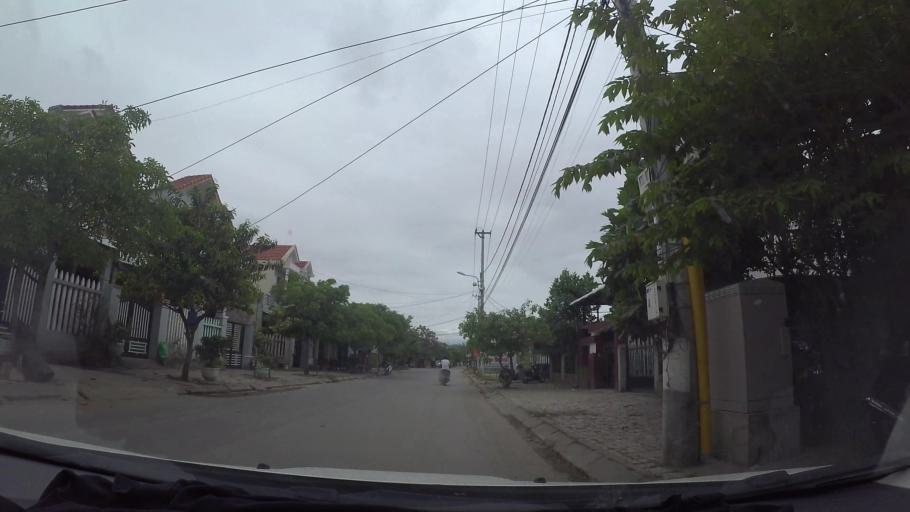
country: VN
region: Da Nang
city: Lien Chieu
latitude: 16.0944
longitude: 108.1035
